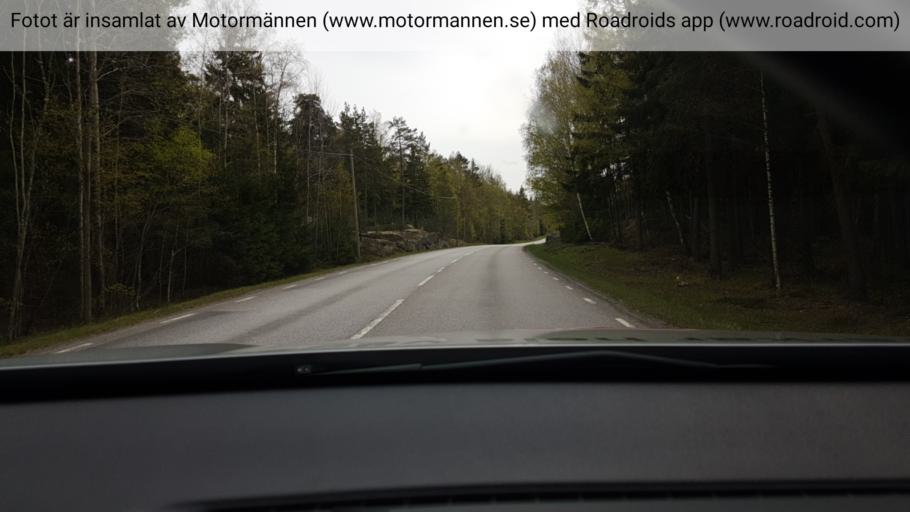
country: SE
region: Stockholm
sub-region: Vallentuna Kommun
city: Vallentuna
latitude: 59.7713
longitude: 18.0428
